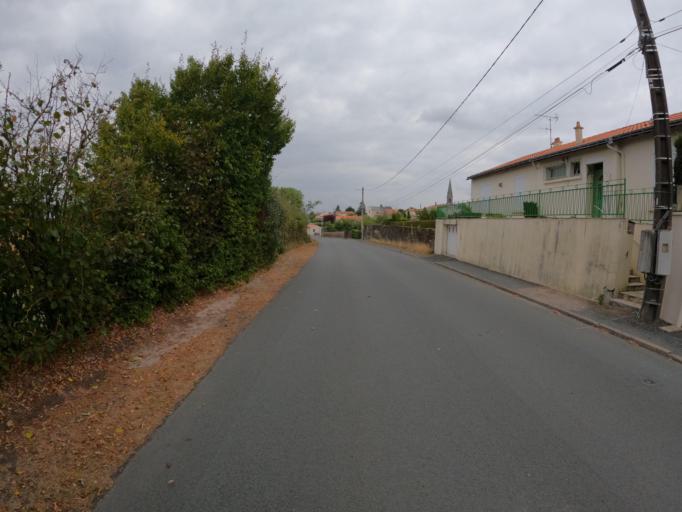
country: FR
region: Pays de la Loire
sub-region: Departement de la Vendee
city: Tiffauges
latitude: 47.0113
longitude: -1.1153
